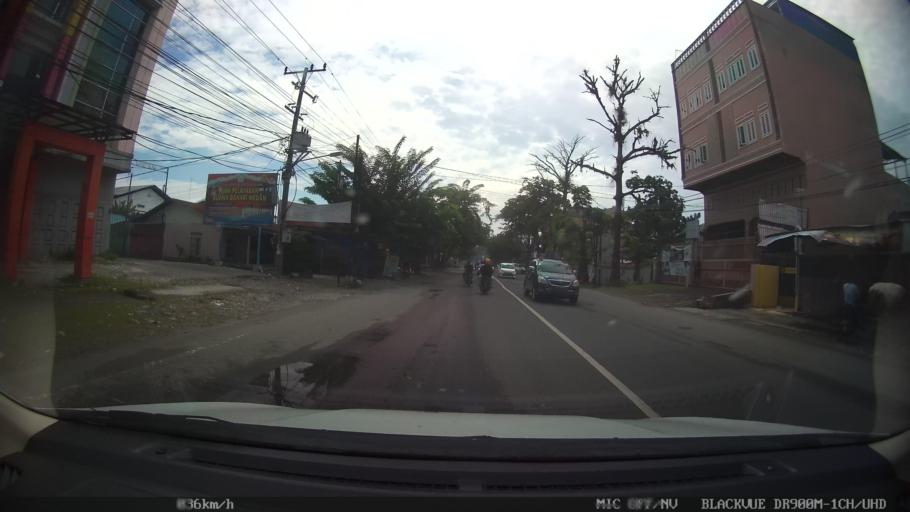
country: ID
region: North Sumatra
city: Medan
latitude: 3.6225
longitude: 98.6884
